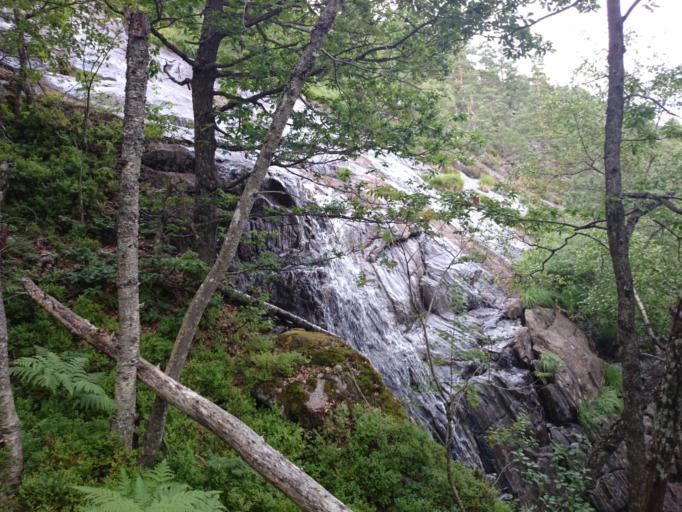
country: NO
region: Aust-Agder
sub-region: Amli
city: Amli
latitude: 58.7691
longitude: 8.4636
